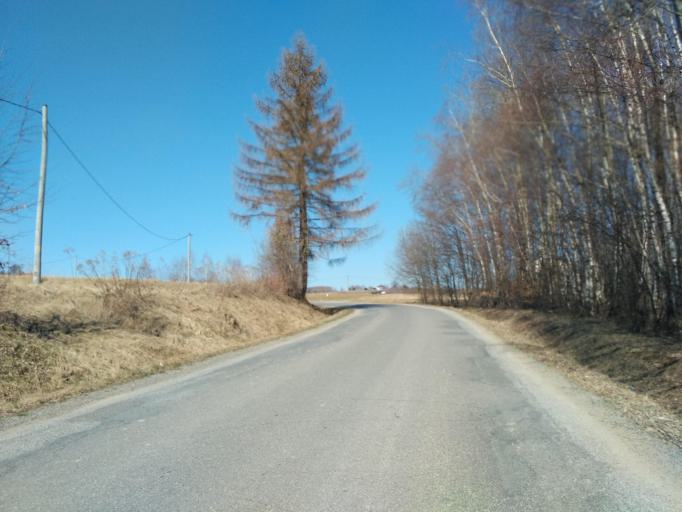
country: PL
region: Subcarpathian Voivodeship
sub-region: Powiat debicki
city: Brzostek
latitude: 49.9553
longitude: 21.4301
